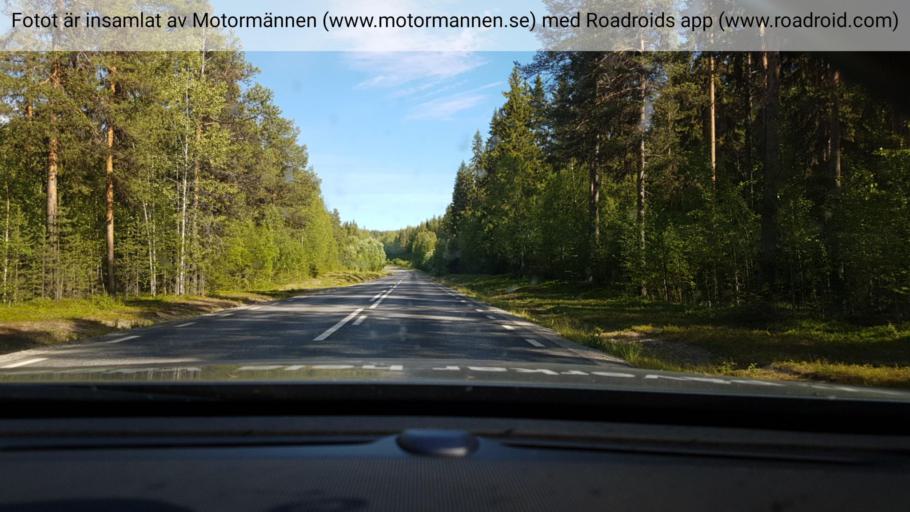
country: SE
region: Vaesterbotten
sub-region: Lycksele Kommun
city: Soderfors
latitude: 64.7068
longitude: 18.3168
